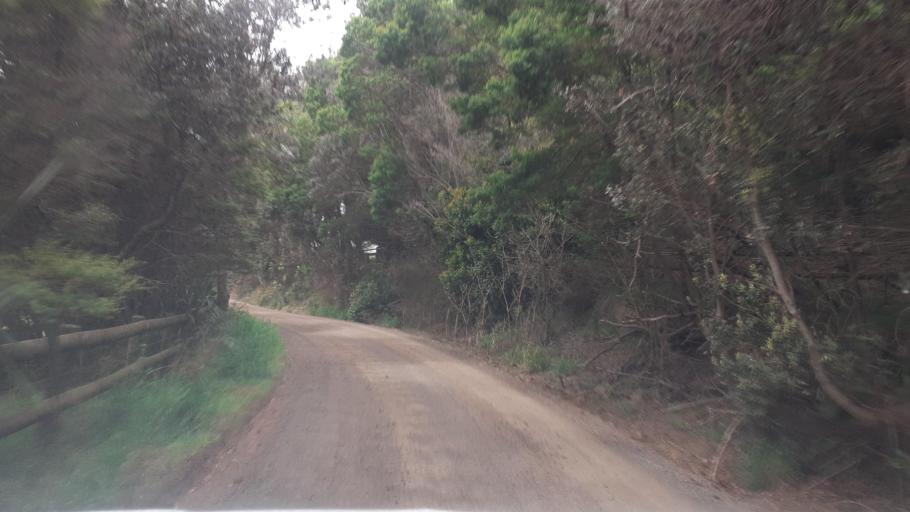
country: NZ
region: Northland
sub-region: Far North District
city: Kerikeri
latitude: -35.1042
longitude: 173.9272
